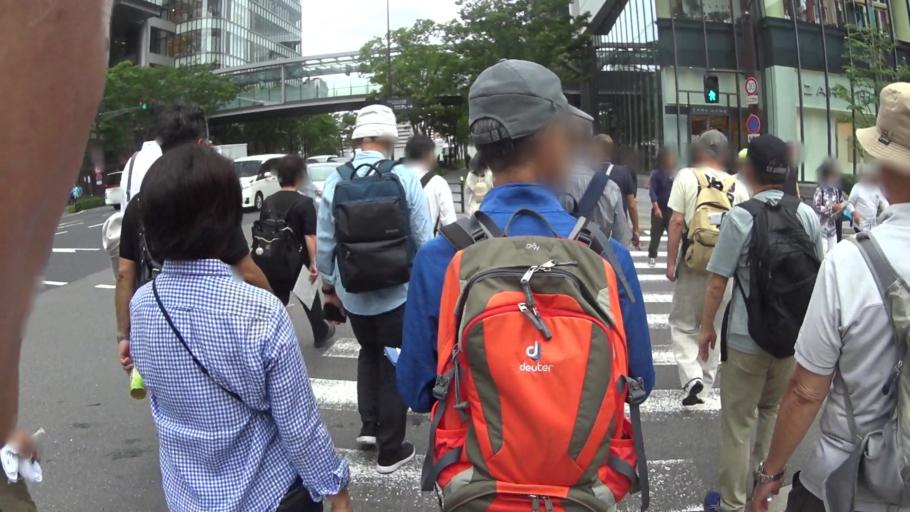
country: JP
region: Osaka
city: Osaka-shi
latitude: 34.7048
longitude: 135.4955
